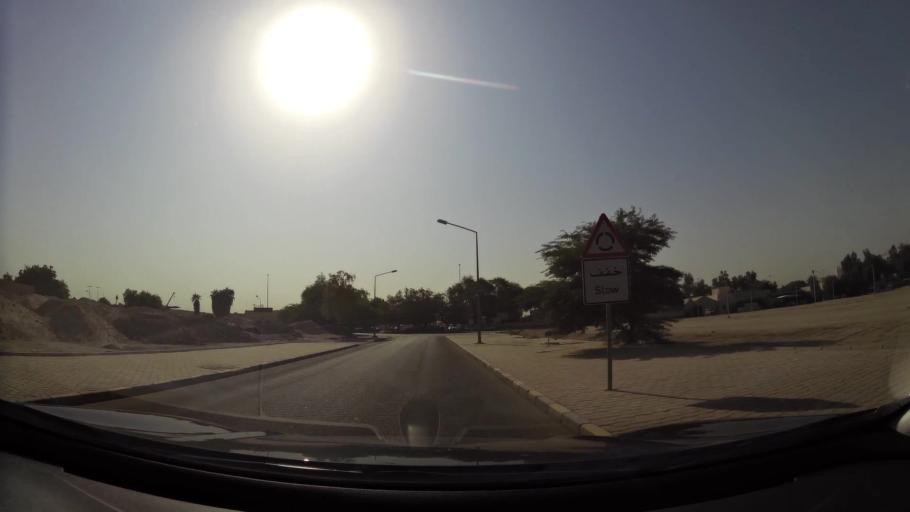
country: KW
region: Al Asimah
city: Ash Shamiyah
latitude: 29.3557
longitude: 47.9480
